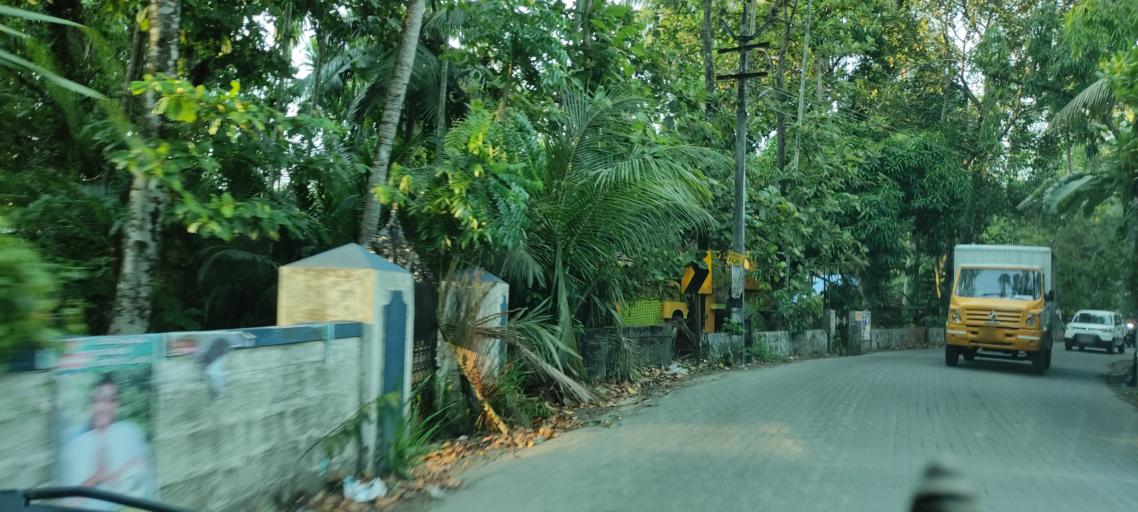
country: IN
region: Kerala
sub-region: Alappuzha
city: Arukutti
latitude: 9.8691
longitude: 76.3117
